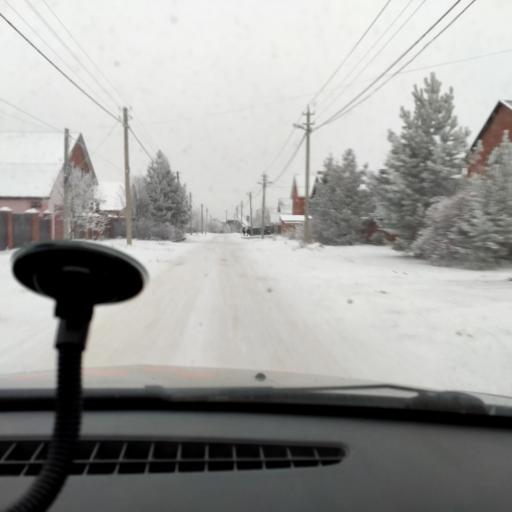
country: RU
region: Bashkortostan
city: Ufa
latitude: 54.6027
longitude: 55.9310
